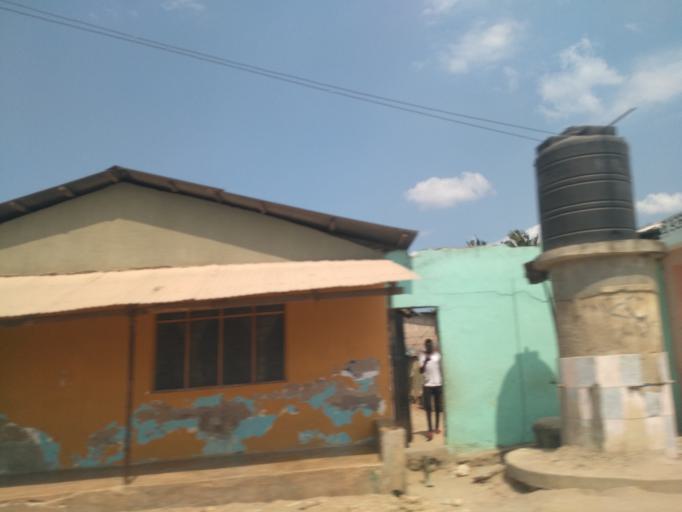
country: TZ
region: Dar es Salaam
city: Dar es Salaam
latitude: -6.8229
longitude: 39.3057
